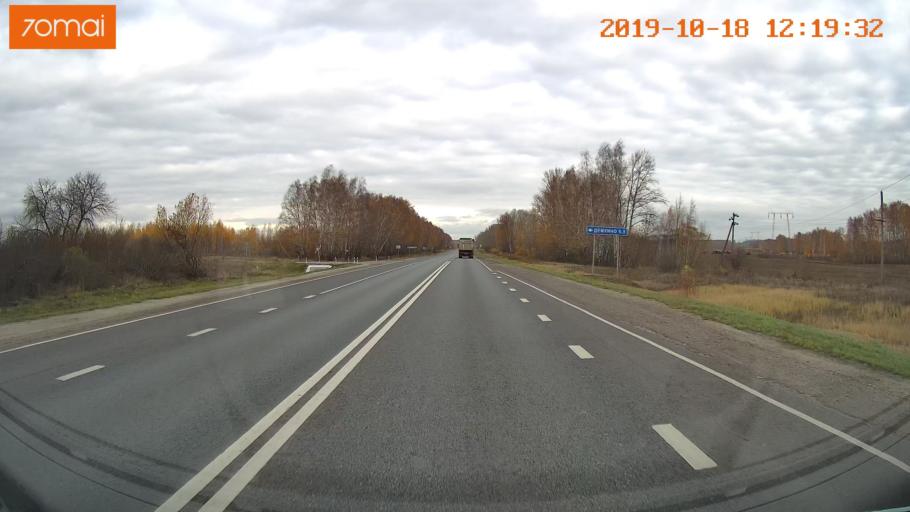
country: RU
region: Rjazan
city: Zakharovo
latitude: 54.4838
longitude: 39.4693
